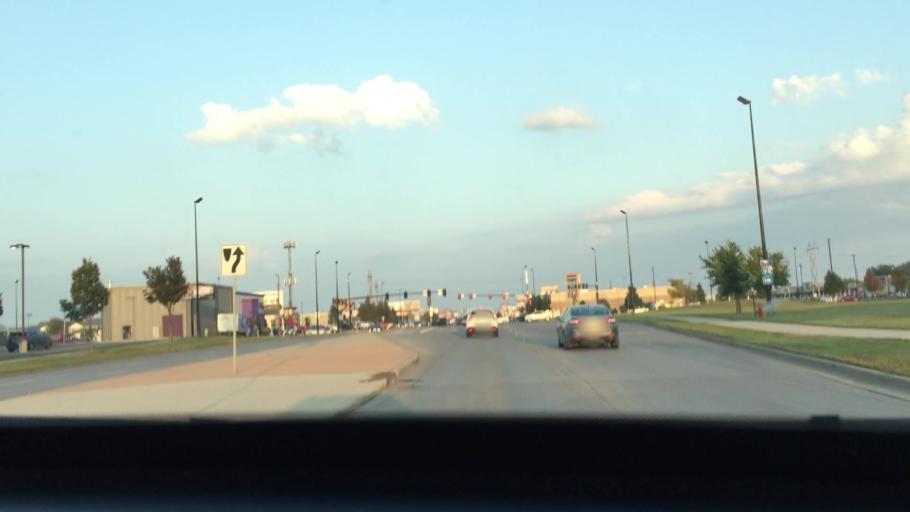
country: US
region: North Dakota
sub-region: Cass County
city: West Fargo
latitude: 46.8618
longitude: -96.8644
